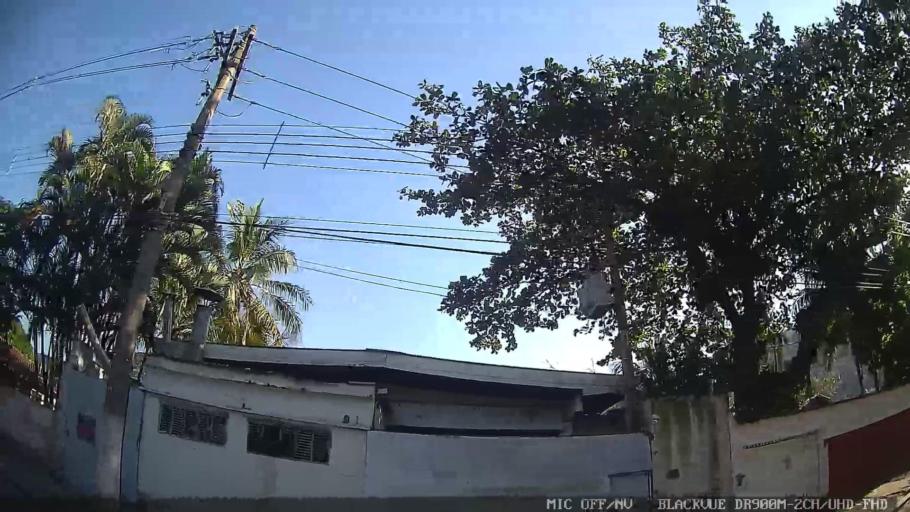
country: BR
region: Sao Paulo
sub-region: Guaruja
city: Guaruja
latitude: -24.0156
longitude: -46.2898
